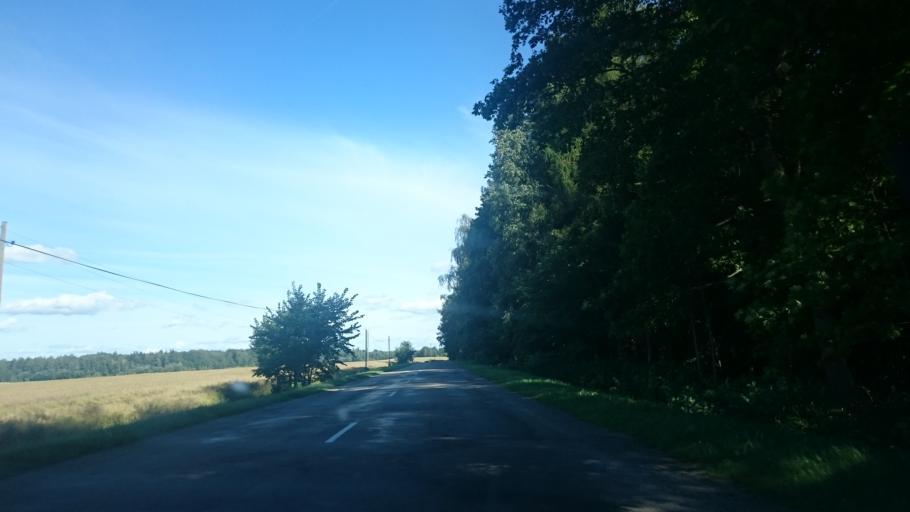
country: LV
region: Aizpute
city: Aizpute
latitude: 56.7277
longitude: 21.7410
